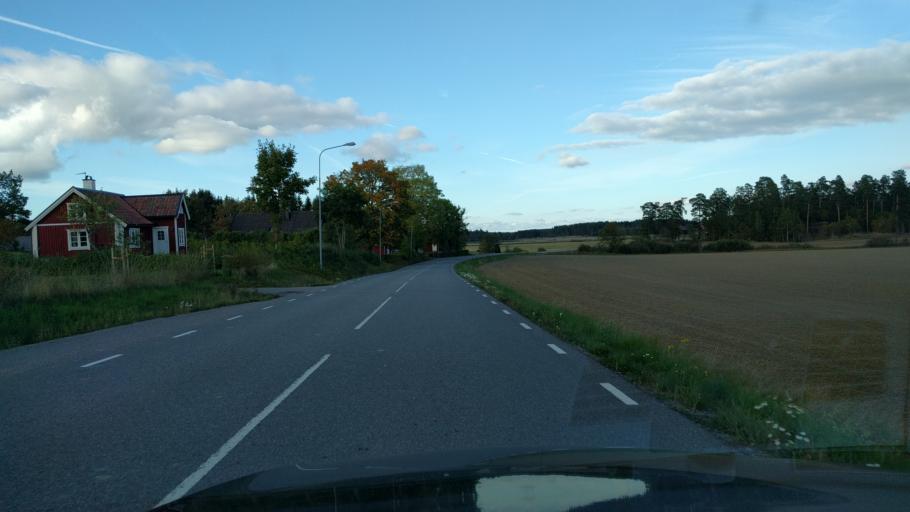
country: SE
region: Uppsala
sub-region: Tierps Kommun
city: Orbyhus
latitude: 60.1729
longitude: 17.6144
